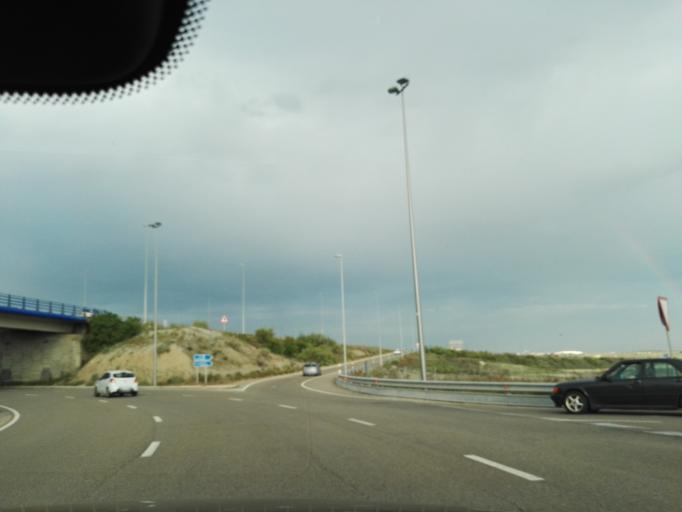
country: ES
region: Aragon
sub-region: Provincia de Zaragoza
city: Montecanal
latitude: 41.6193
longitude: -0.9611
